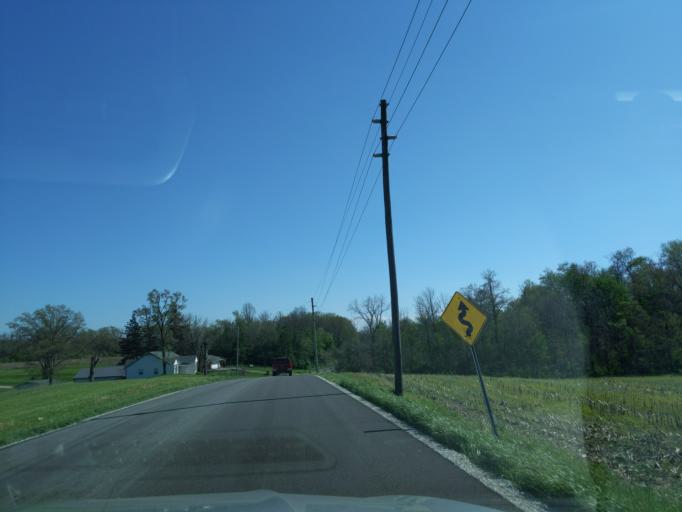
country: US
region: Indiana
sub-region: Decatur County
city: Greensburg
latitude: 39.3087
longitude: -85.4903
